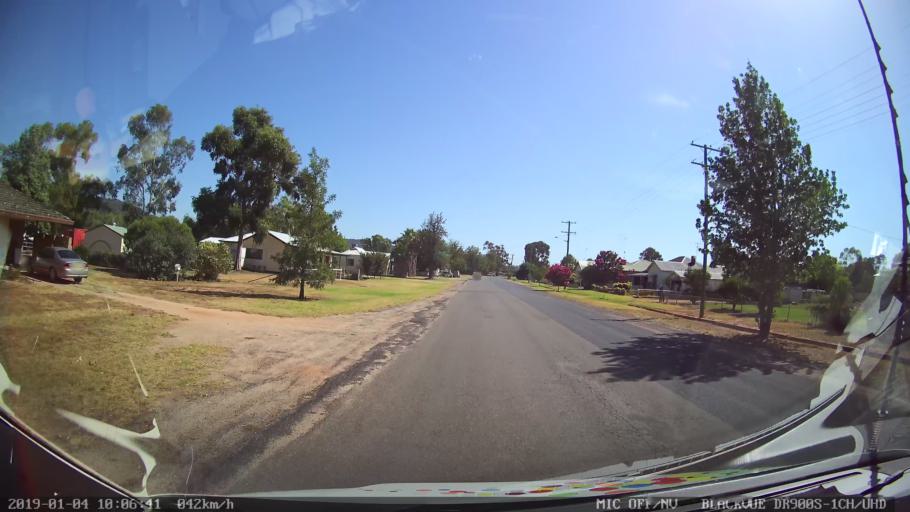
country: AU
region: New South Wales
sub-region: Cabonne
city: Canowindra
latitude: -33.4324
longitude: 148.3695
